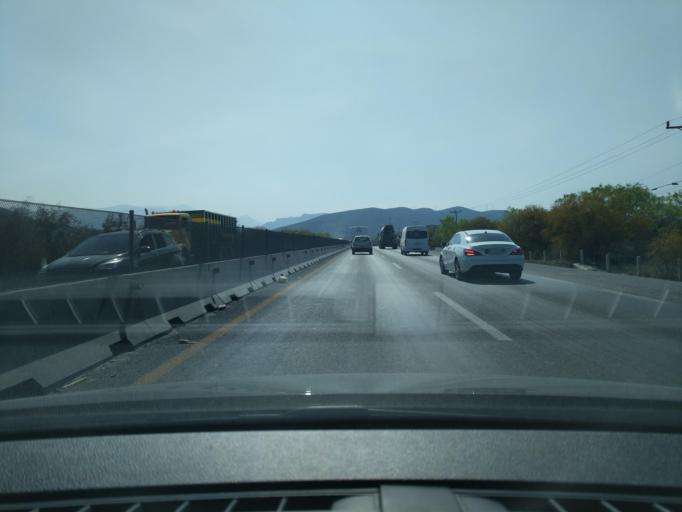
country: MX
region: Nuevo Leon
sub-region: Garcia
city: Los Parques
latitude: 25.7713
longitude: -100.4744
